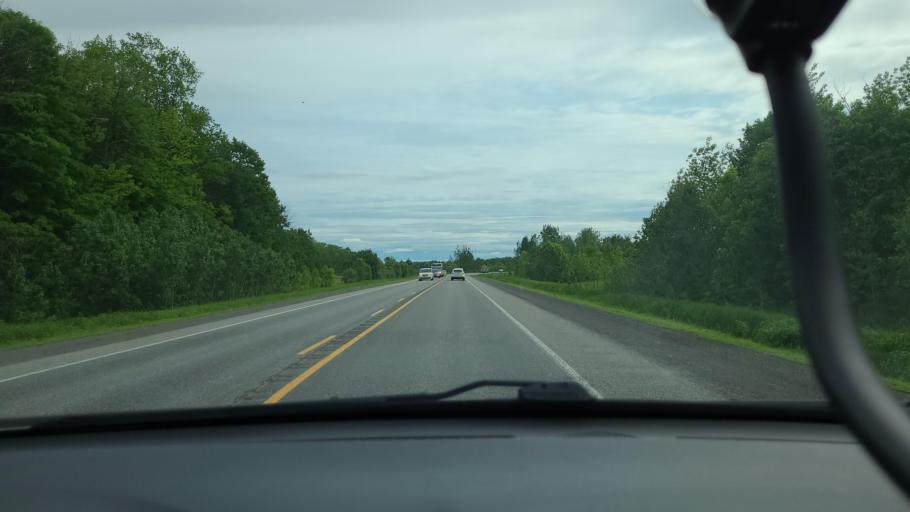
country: CA
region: Quebec
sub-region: Lanaudiere
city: Saint-Jacques
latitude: 45.9704
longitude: -73.5519
